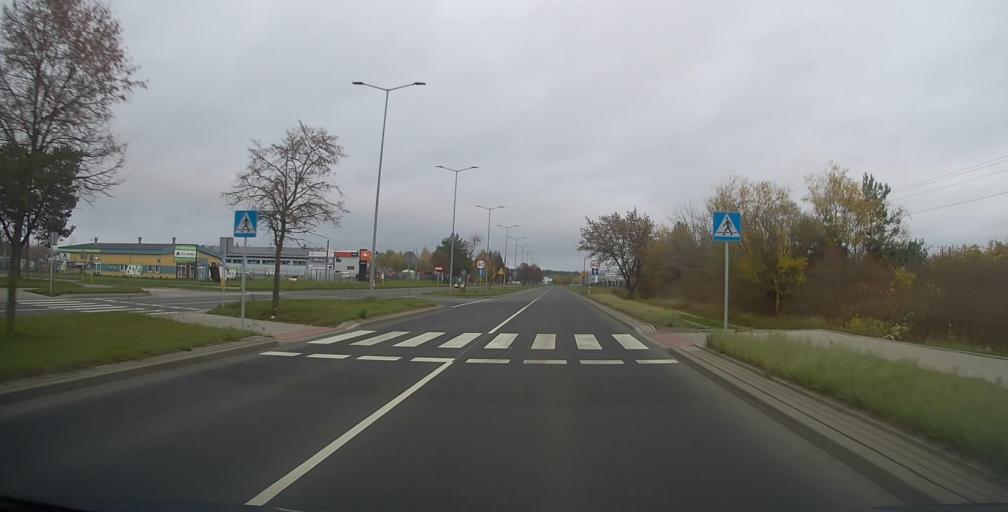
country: PL
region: Warmian-Masurian Voivodeship
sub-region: Powiat elcki
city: Elk
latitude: 53.8252
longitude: 22.3910
